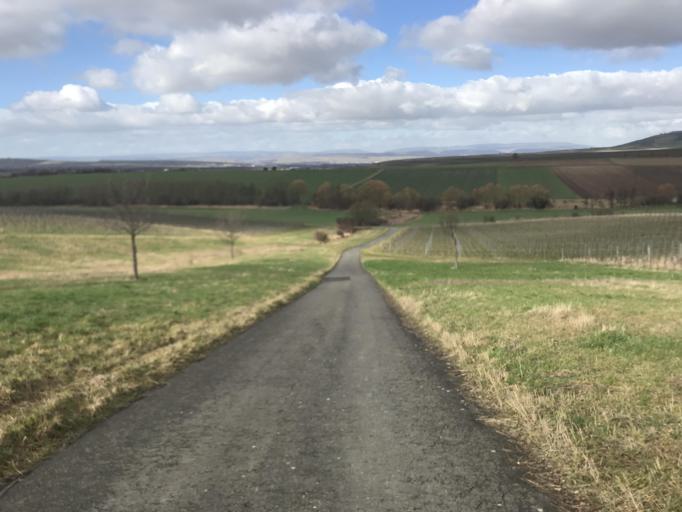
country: DE
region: Rheinland-Pfalz
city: Sankt Johann
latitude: 49.8582
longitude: 8.0128
